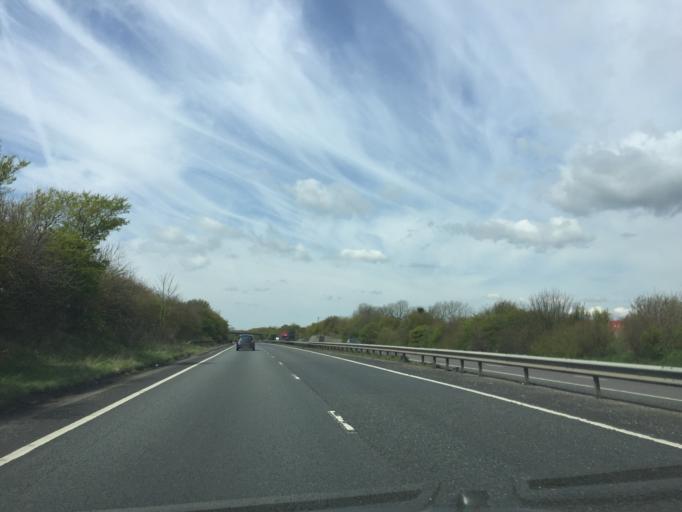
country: GB
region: England
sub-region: Kent
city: Folkestone
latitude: 51.1114
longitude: 1.2221
